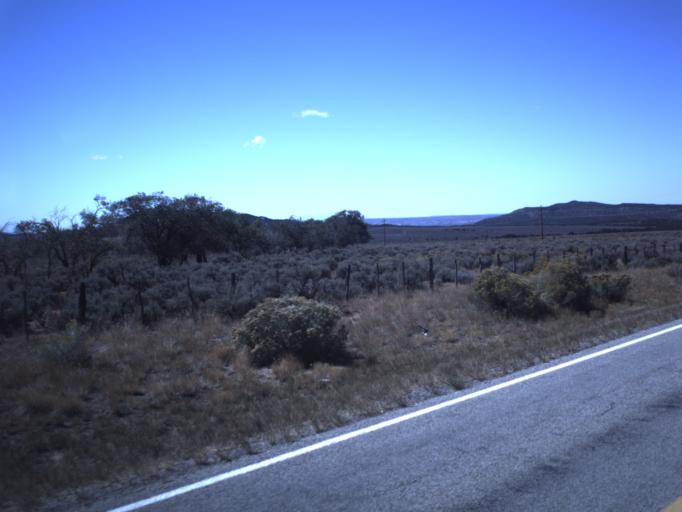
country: US
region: Utah
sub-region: Grand County
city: Moab
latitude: 38.3102
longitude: -109.2961
